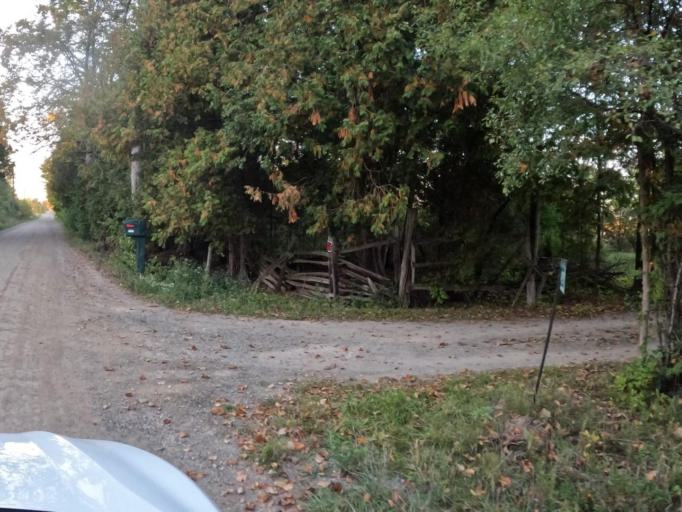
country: CA
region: Ontario
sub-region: Wellington County
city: Guelph
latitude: 43.5653
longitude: -80.1663
